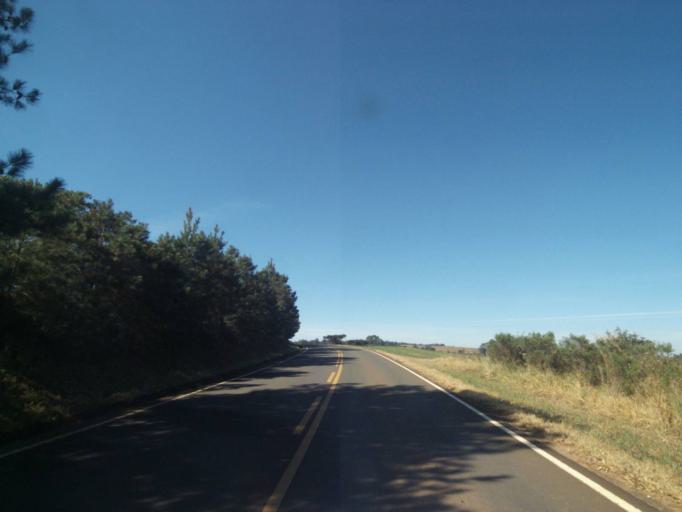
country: BR
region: Parana
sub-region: Tibagi
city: Tibagi
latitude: -24.4919
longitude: -50.4662
